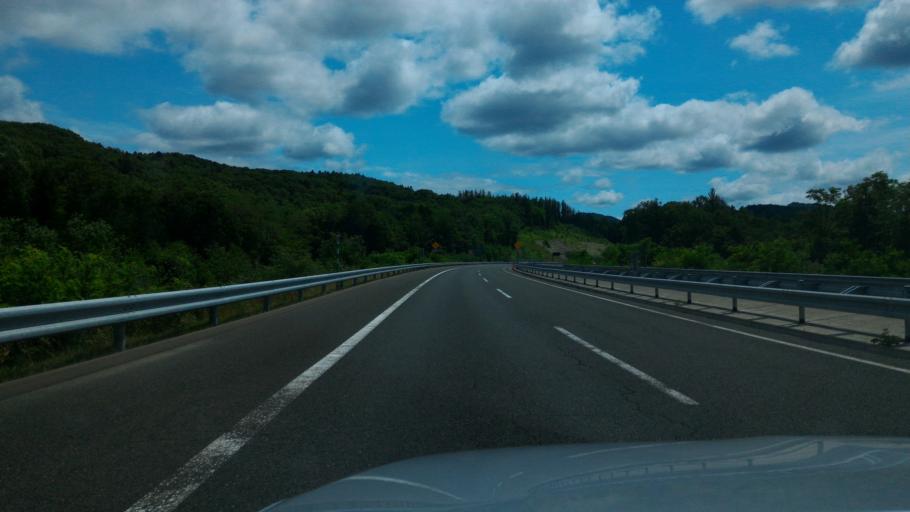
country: JP
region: Hokkaido
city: Shimo-furano
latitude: 42.9892
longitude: 142.4113
